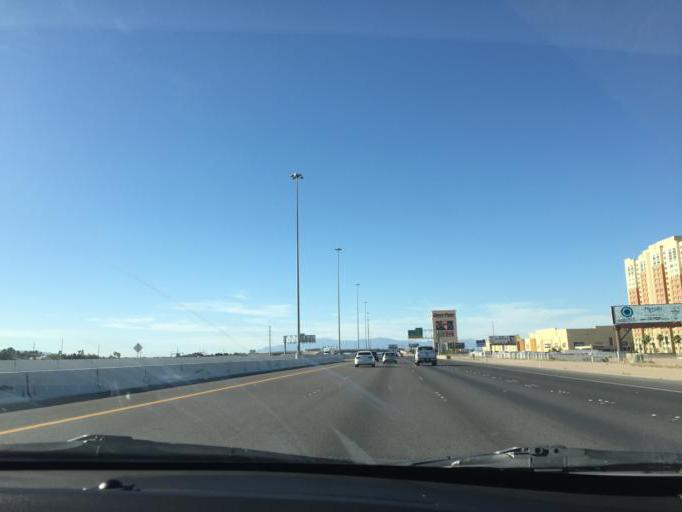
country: US
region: Nevada
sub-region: Clark County
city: Enterprise
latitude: 36.0061
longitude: -115.1803
